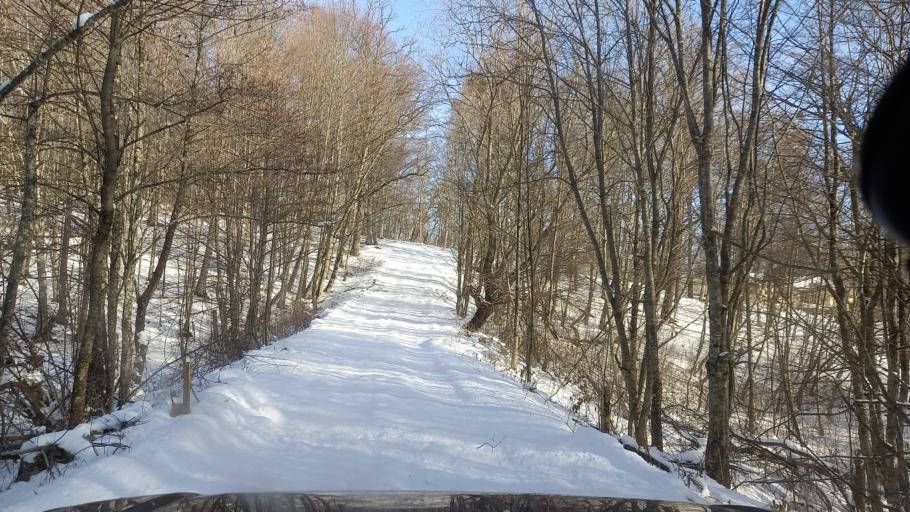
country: RU
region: Adygeya
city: Kamennomostskiy
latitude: 44.2312
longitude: 40.0960
